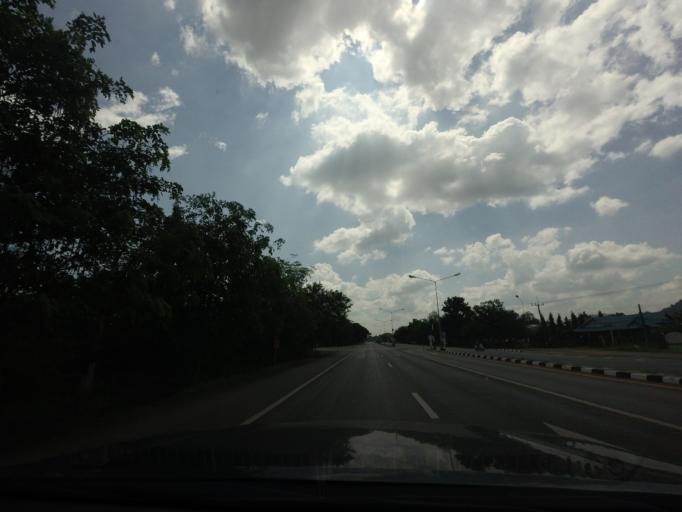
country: TH
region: Phetchabun
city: Nong Phai
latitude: 16.1258
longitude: 101.0412
